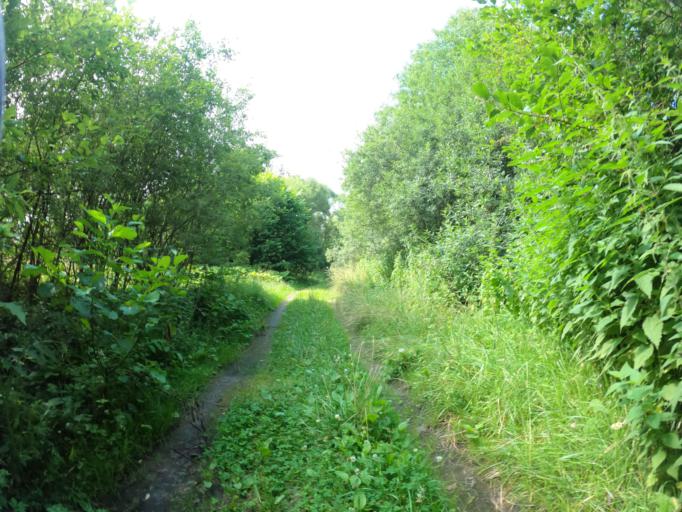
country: PL
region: West Pomeranian Voivodeship
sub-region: Powiat szczecinecki
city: Grzmiaca
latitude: 53.8313
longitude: 16.4479
